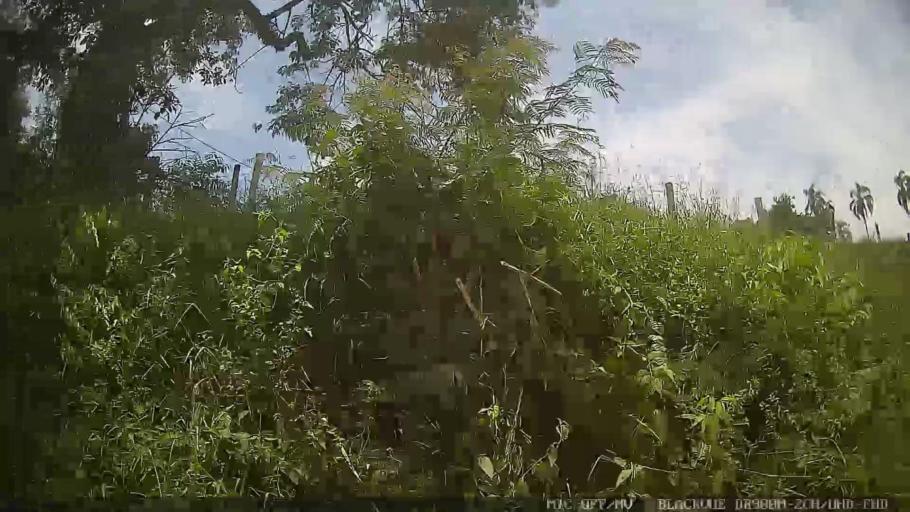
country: BR
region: Sao Paulo
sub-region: Santa Isabel
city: Santa Isabel
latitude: -23.3432
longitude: -46.1970
